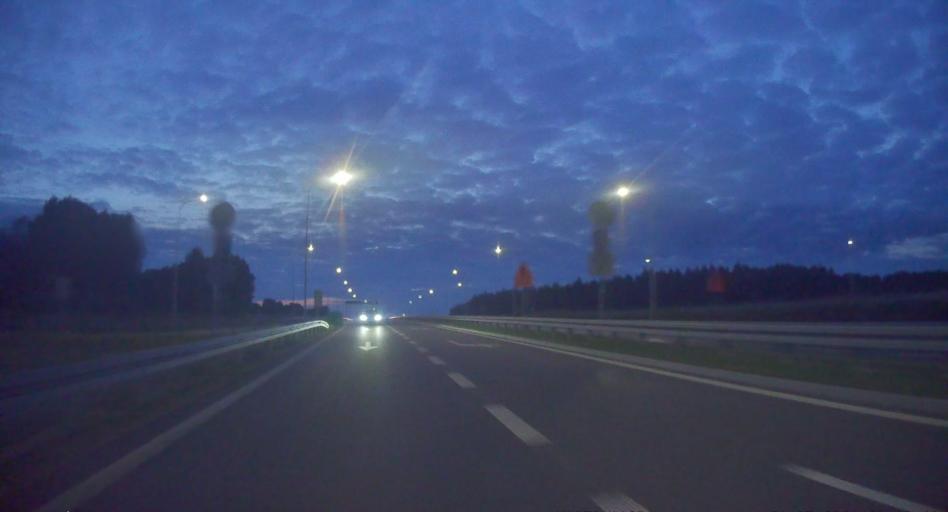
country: PL
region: Silesian Voivodeship
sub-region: Powiat klobucki
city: Kamyk
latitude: 50.8525
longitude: 19.0360
